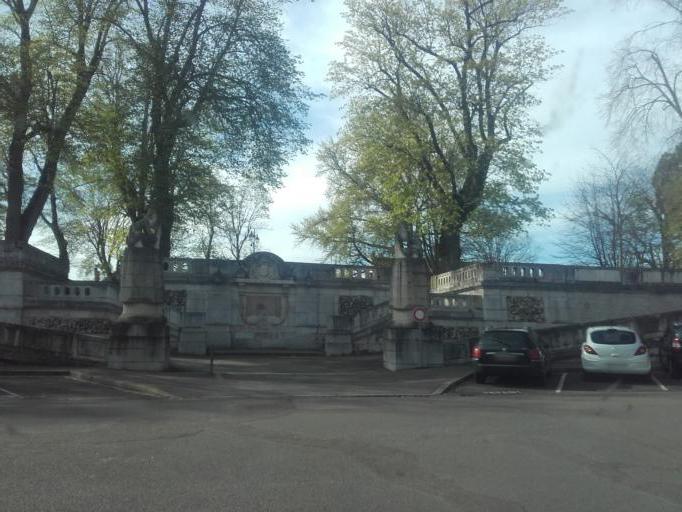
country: FR
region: Bourgogne
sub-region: Departement de la Cote-d'Or
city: Beaune
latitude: 47.0254
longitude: 4.8355
